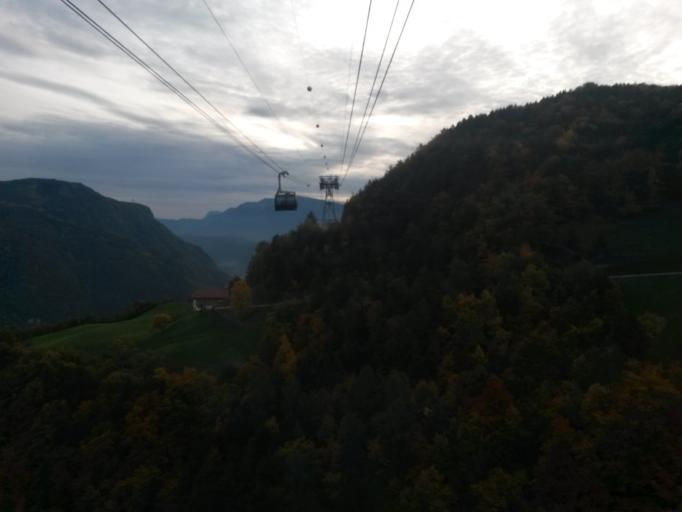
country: IT
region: Trentino-Alto Adige
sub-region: Bolzano
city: Cardano
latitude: 46.5138
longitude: 11.3843
